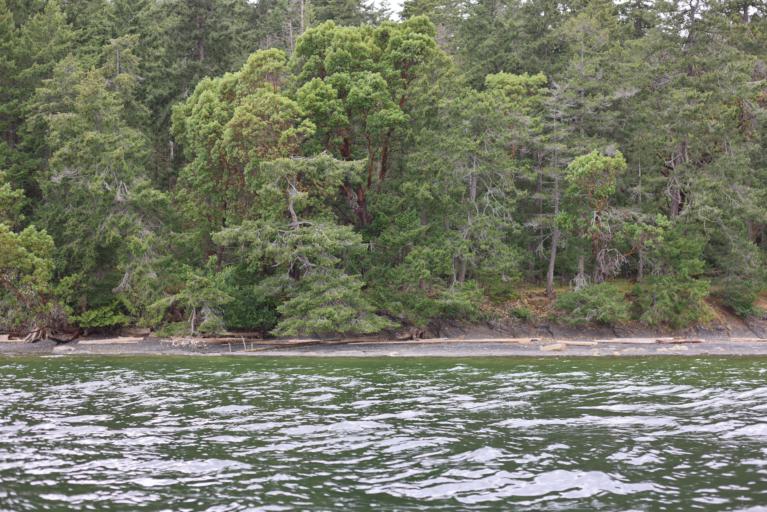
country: CA
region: British Columbia
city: North Cowichan
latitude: 48.9016
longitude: -123.6639
